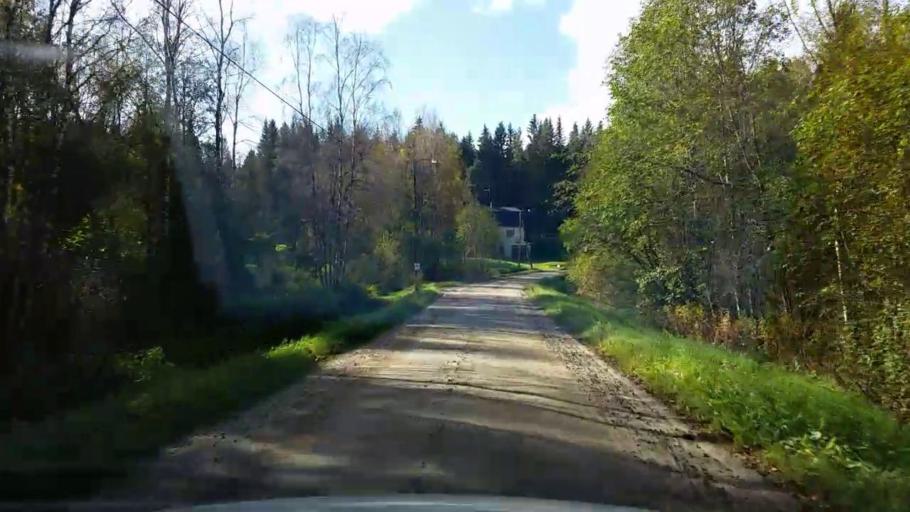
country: SE
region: Gaevleborg
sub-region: Ljusdals Kommun
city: Jaervsoe
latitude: 61.7905
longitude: 16.1986
